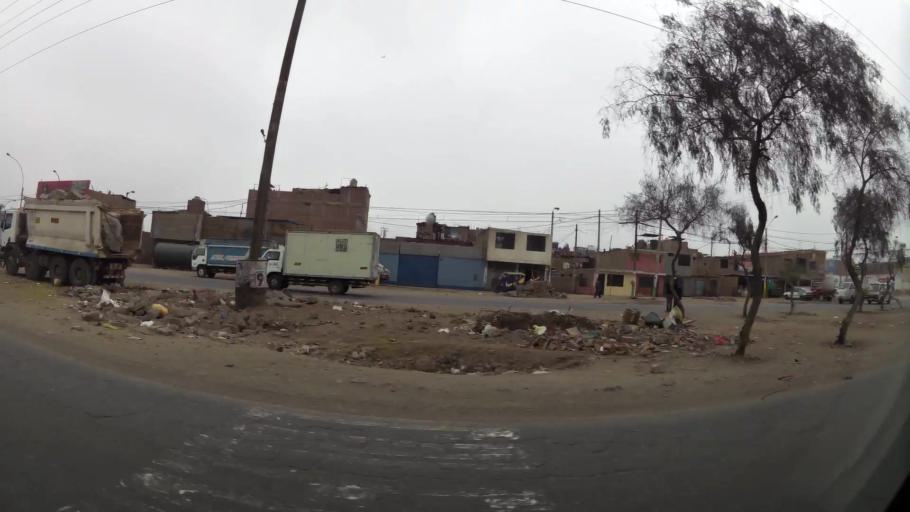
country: PE
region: Lima
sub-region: Lima
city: Urb. Santo Domingo
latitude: -11.9217
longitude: -77.0623
